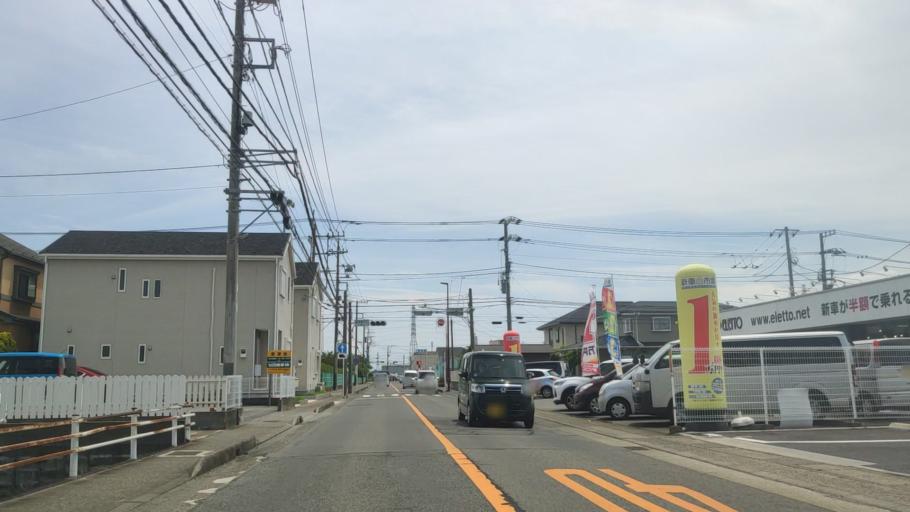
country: JP
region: Kanagawa
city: Chigasaki
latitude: 35.3625
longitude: 139.3853
